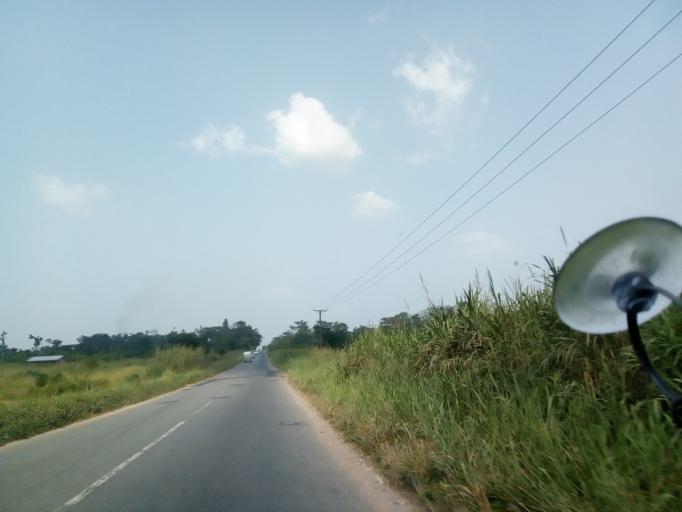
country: GH
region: Eastern
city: Suhum
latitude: 6.0530
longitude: -0.4065
